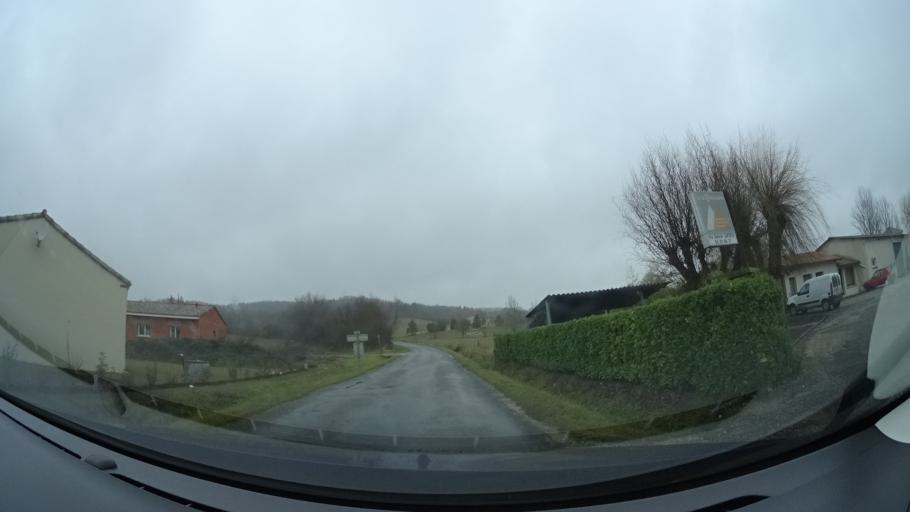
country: FR
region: Midi-Pyrenees
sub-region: Departement du Lot
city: Montcuq
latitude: 44.3584
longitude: 1.2307
